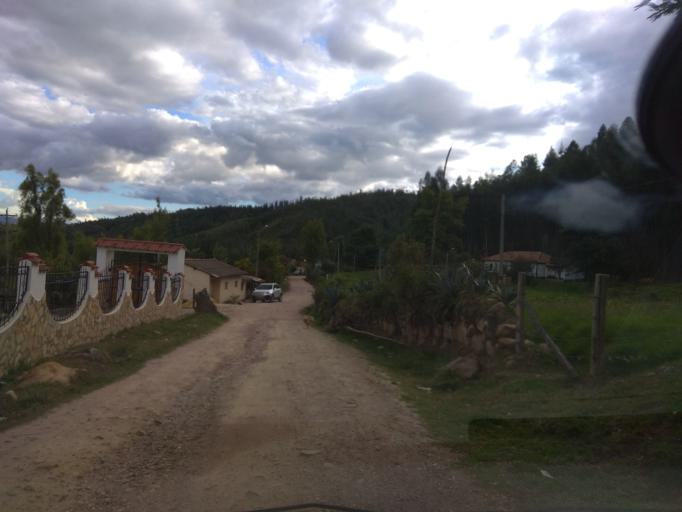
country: CO
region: Boyaca
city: Paipa
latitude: 5.8022
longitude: -73.1086
